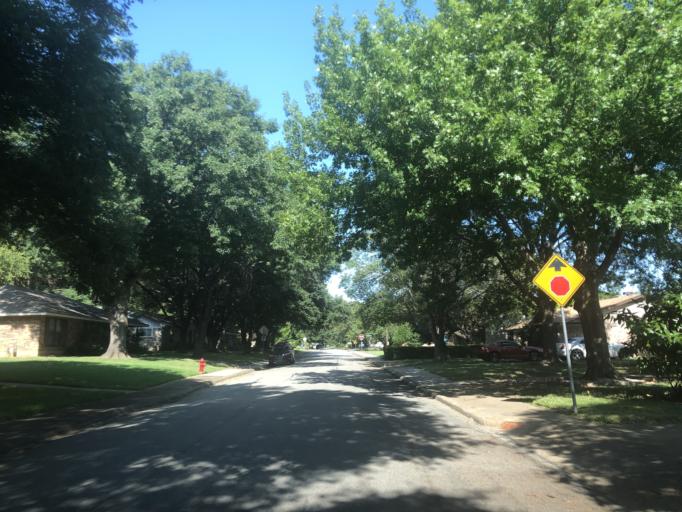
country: US
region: Texas
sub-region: Dallas County
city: Grand Prairie
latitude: 32.7530
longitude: -97.0210
